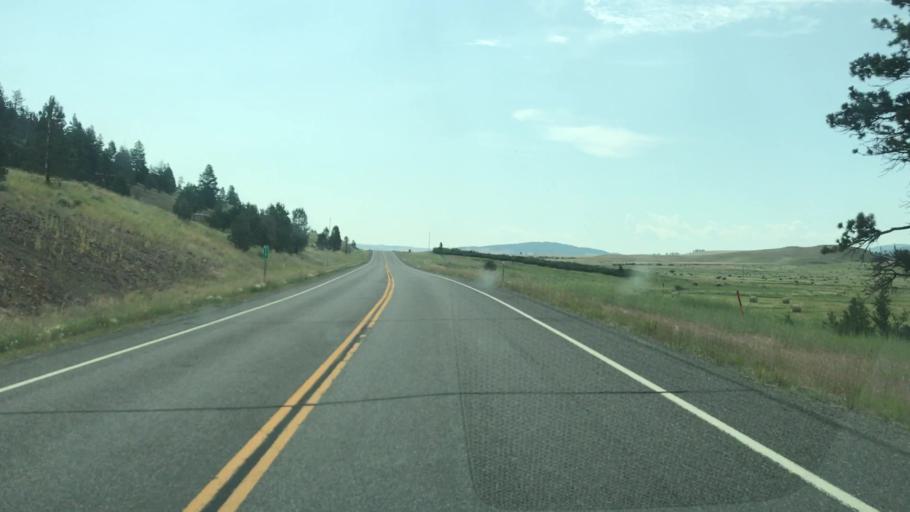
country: US
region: Montana
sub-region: Lewis and Clark County
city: Lincoln
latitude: 46.7829
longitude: -112.7698
